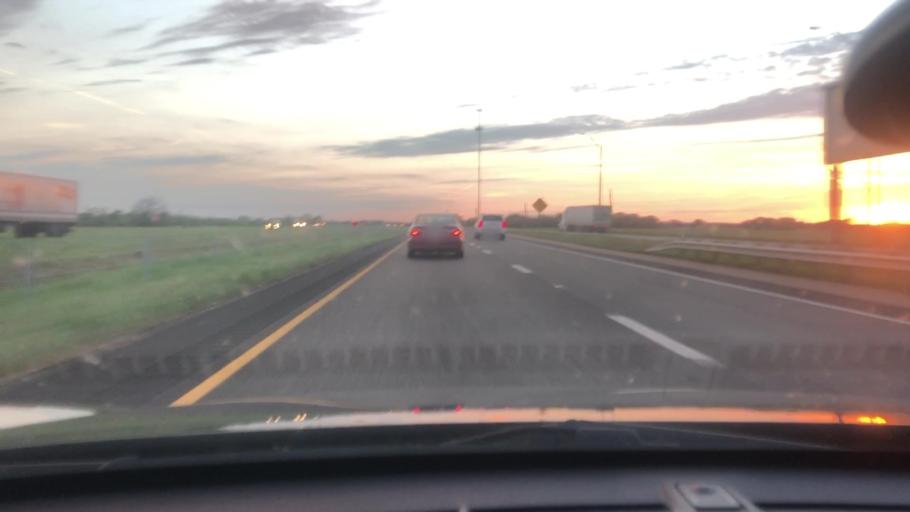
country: US
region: Texas
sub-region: Victoria County
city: Inez
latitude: 28.9274
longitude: -96.7478
